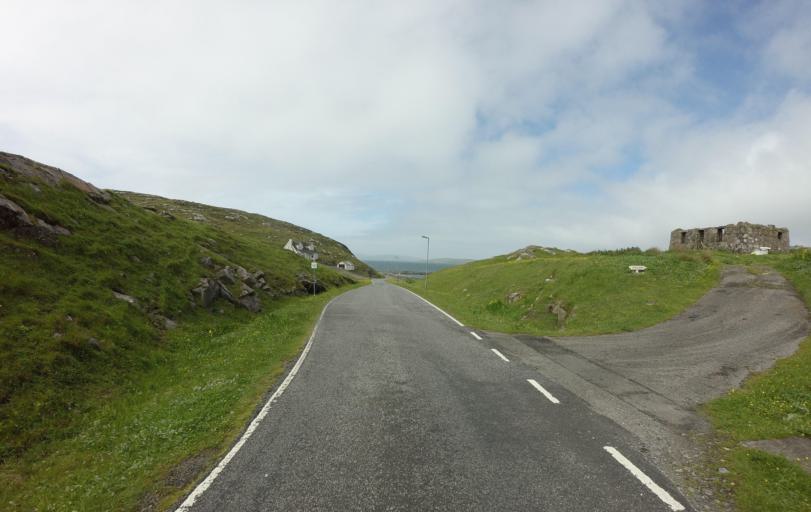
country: GB
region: Scotland
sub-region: Eilean Siar
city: Isle of South Uist
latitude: 57.0727
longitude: -7.3028
